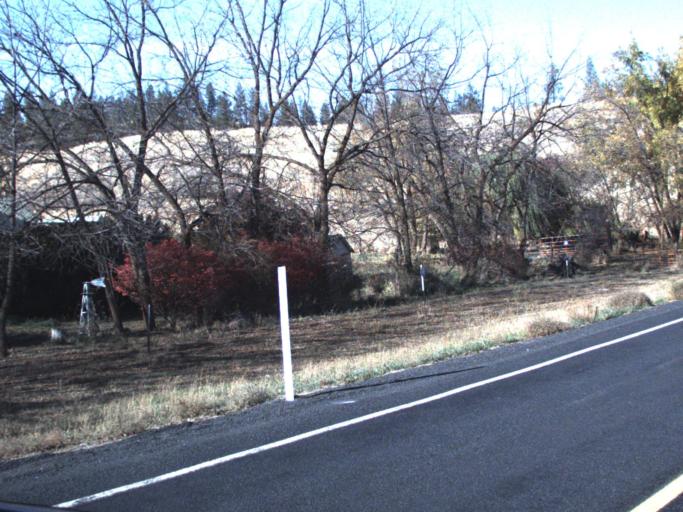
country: US
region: Washington
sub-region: Lincoln County
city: Davenport
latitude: 47.8835
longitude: -118.2644
